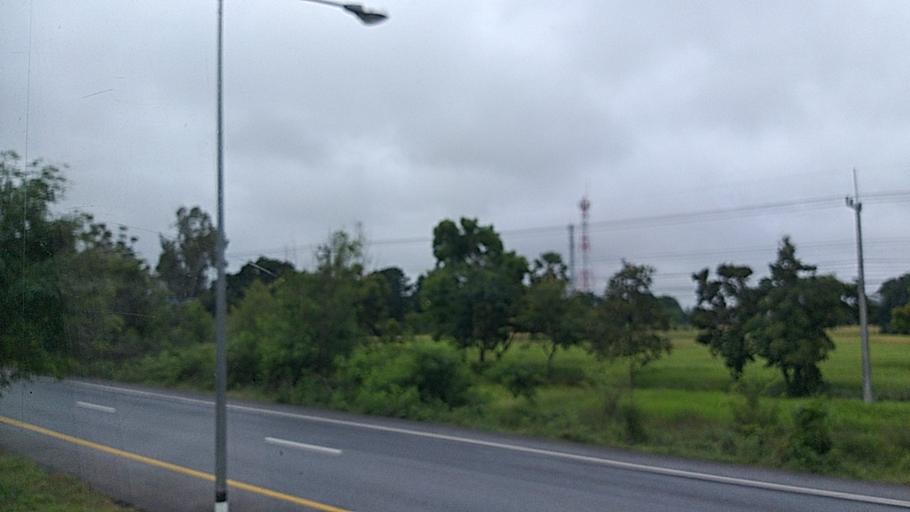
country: TH
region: Nakhon Ratchasima
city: Non Daeng
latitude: 15.3802
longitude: 102.4623
